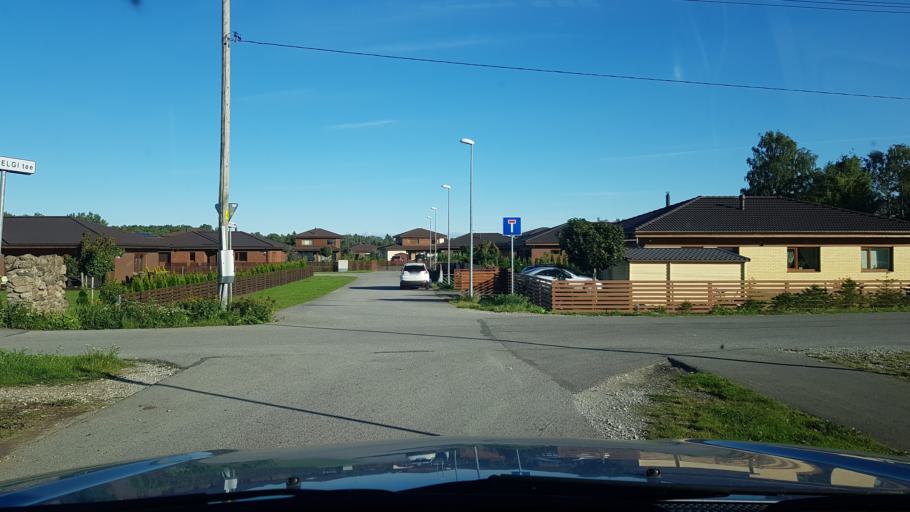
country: EE
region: Harju
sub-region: Rae vald
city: Jueri
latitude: 59.3901
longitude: 24.8541
